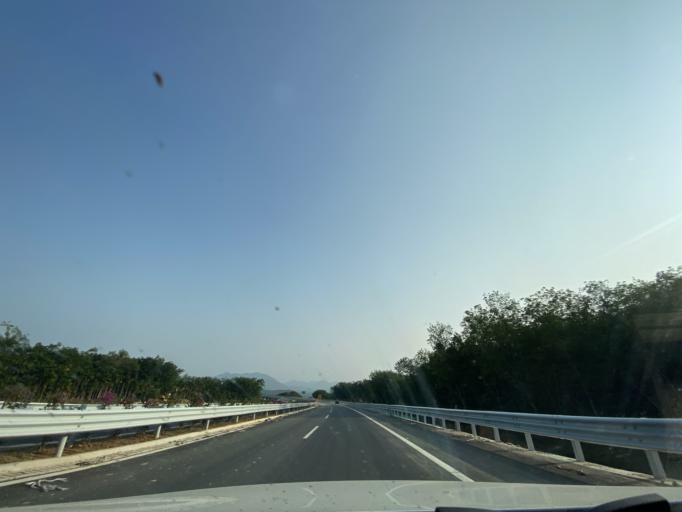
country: CN
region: Hainan
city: Xiangshui
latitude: 18.6430
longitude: 109.6291
